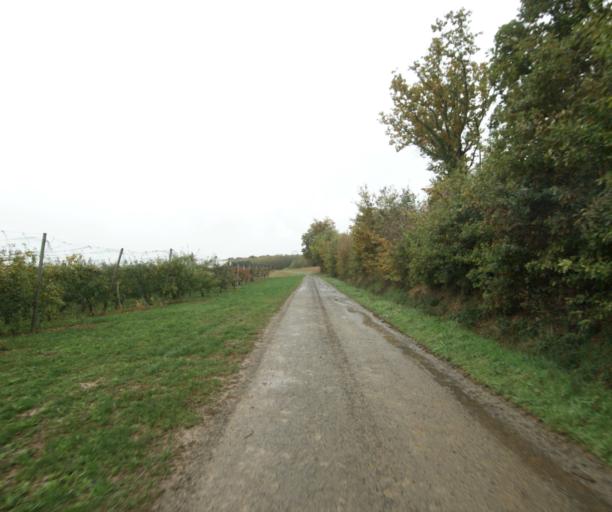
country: FR
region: Rhone-Alpes
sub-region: Departement de l'Ain
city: Pont-de-Vaux
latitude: 46.4818
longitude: 4.8575
